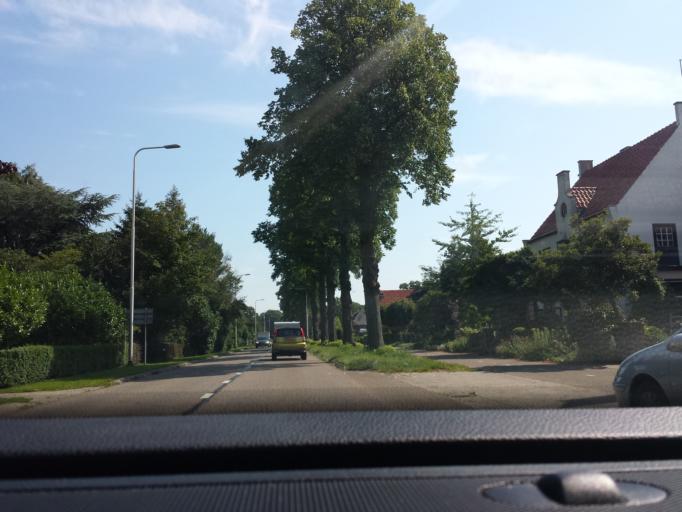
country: NL
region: Gelderland
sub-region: Gemeente Bronckhorst
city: Hengelo
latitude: 52.1049
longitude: 6.3317
